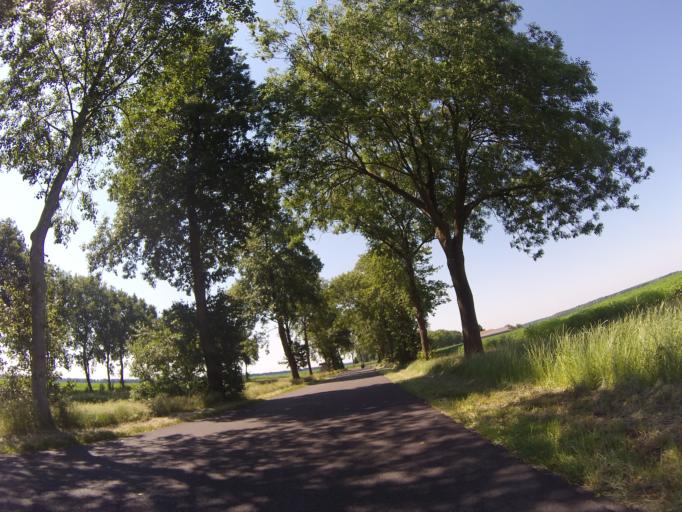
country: NL
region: Drenthe
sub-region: Gemeente Coevorden
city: Sleen
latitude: 52.8265
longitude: 6.8175
